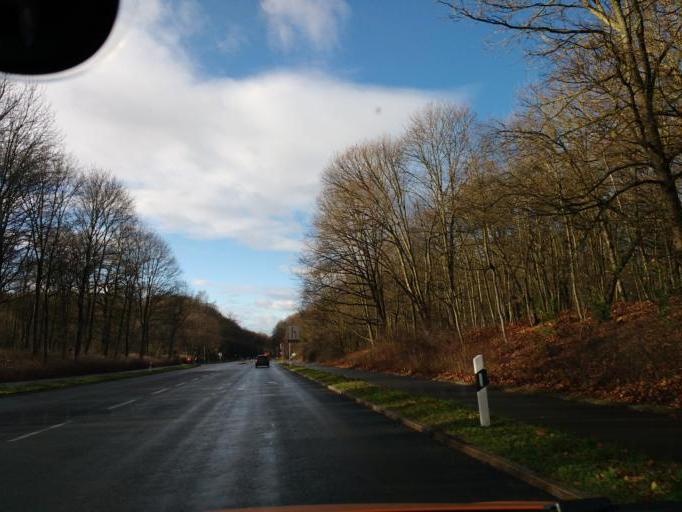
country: DE
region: Berlin
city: Wannsee
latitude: 52.4142
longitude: 13.1113
